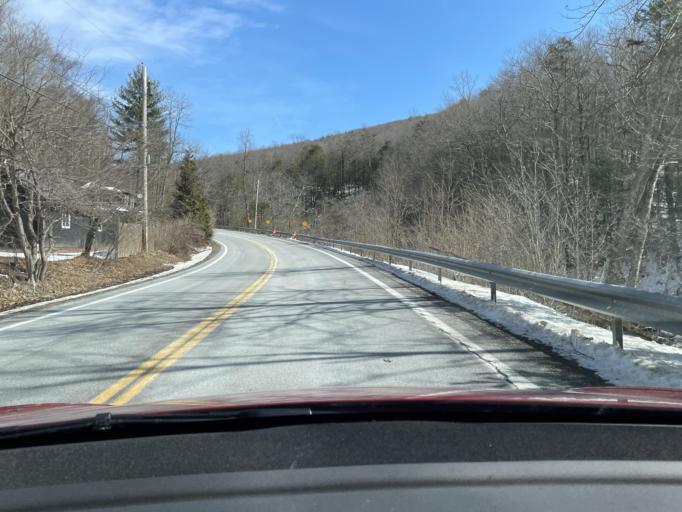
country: US
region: New York
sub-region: Ulster County
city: Shokan
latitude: 42.0571
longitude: -74.2575
